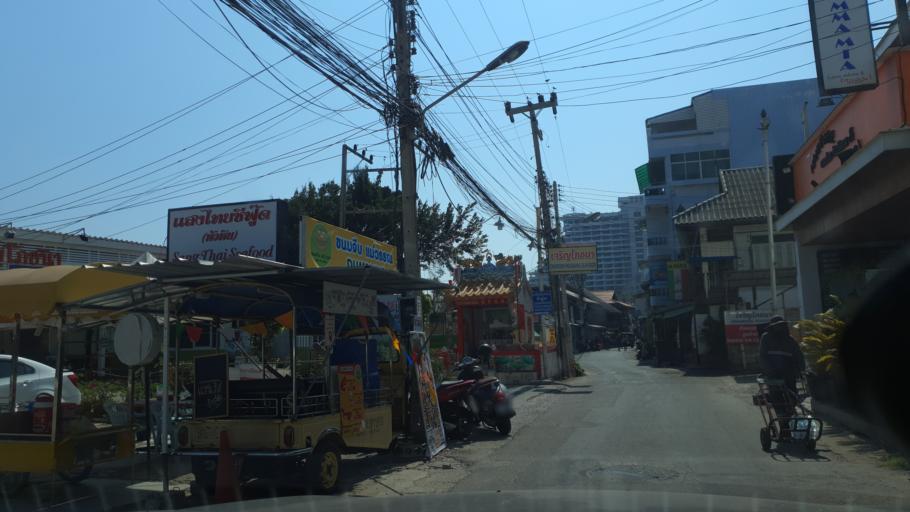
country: TH
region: Prachuap Khiri Khan
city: Hua Hin
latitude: 12.5740
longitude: 99.9590
